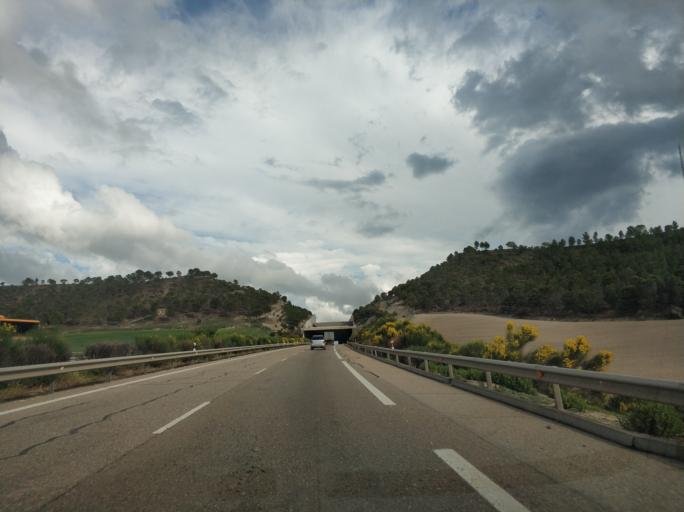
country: ES
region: Castille and Leon
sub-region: Provincia de Valladolid
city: Cisterniga
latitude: 41.6123
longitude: -4.6723
